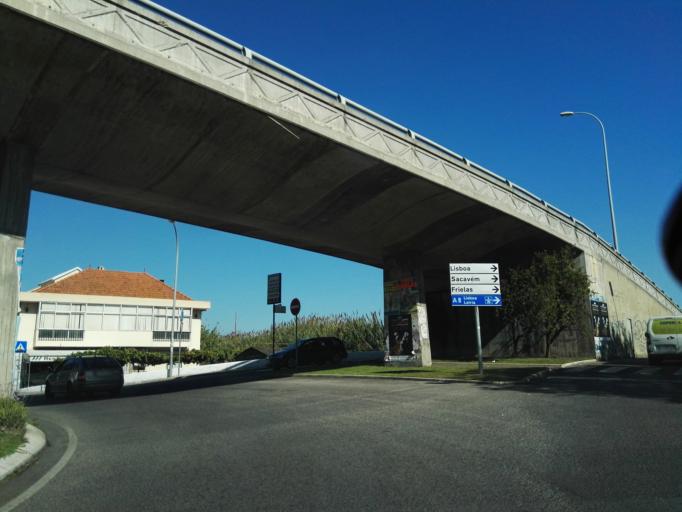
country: PT
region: Lisbon
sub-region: Odivelas
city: Povoa de Santo Adriao
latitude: 38.8155
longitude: -9.1549
